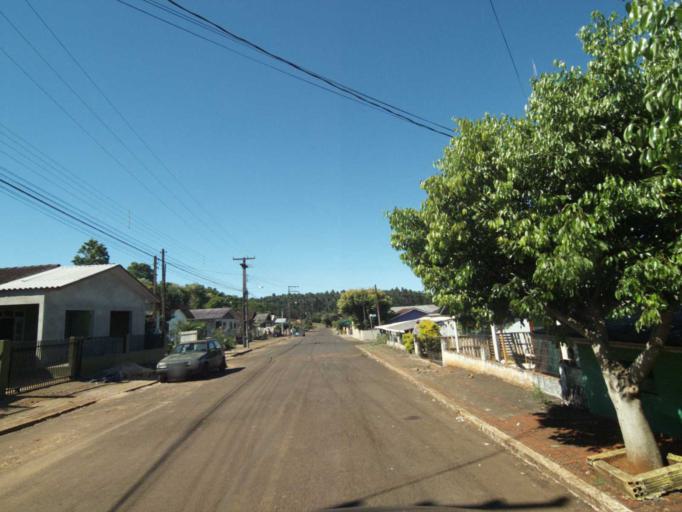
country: BR
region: Parana
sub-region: Coronel Vivida
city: Coronel Vivida
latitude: -25.9588
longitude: -52.8101
